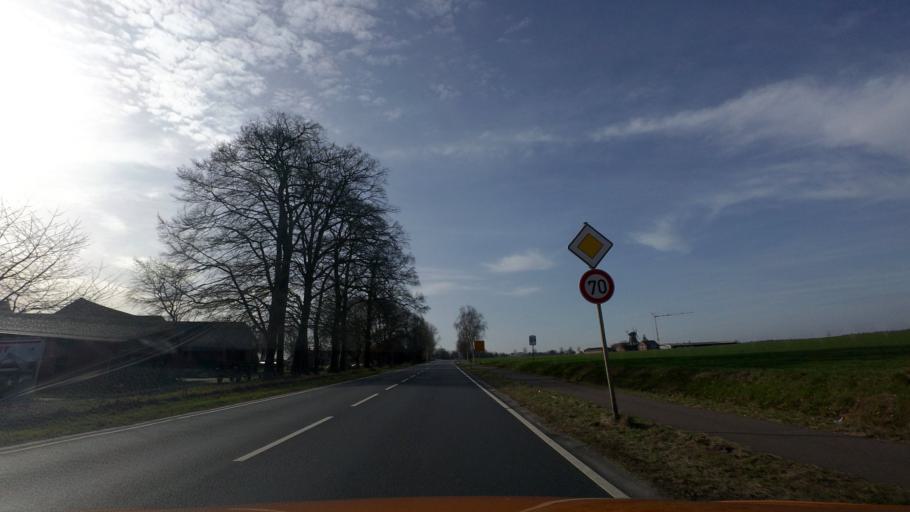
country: DE
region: Lower Saxony
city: Scholen
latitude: 52.7402
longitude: 8.7661
